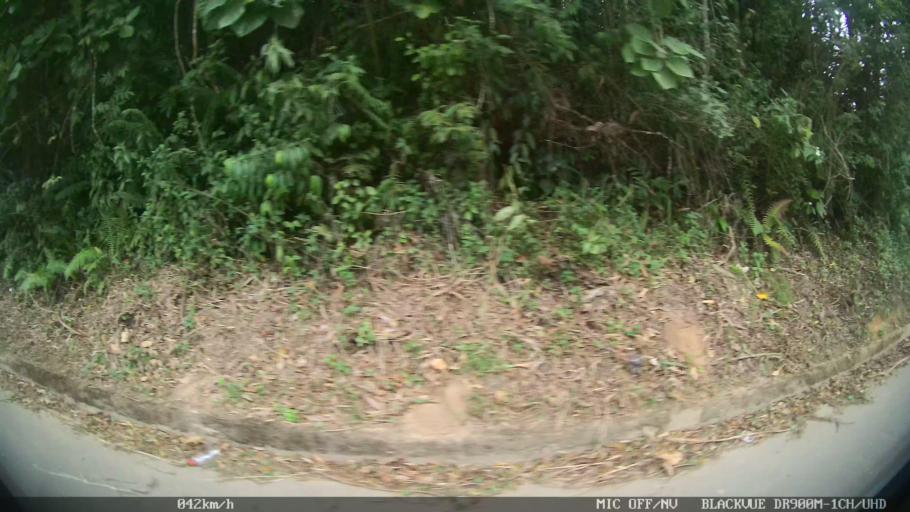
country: BR
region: Santa Catarina
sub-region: Joinville
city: Joinville
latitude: -26.3608
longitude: -48.8474
